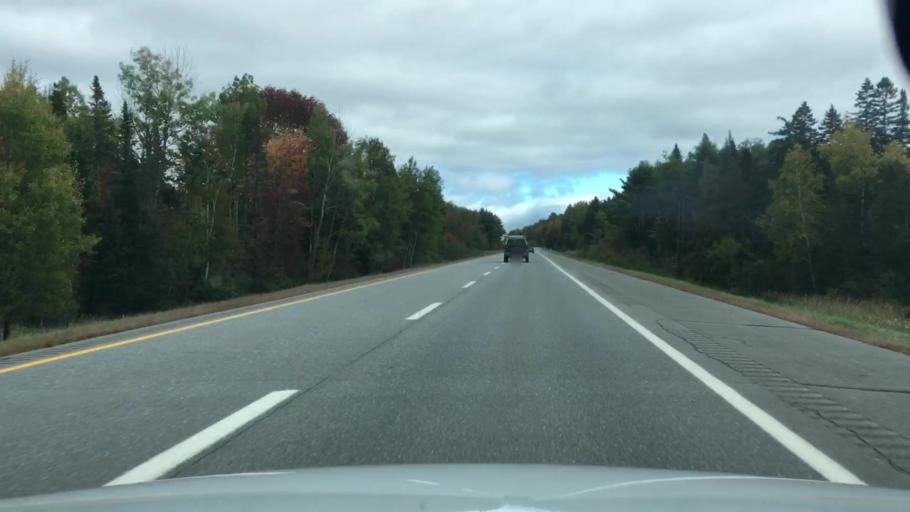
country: US
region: Maine
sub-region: Penobscot County
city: Carmel
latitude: 44.7750
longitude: -69.0402
